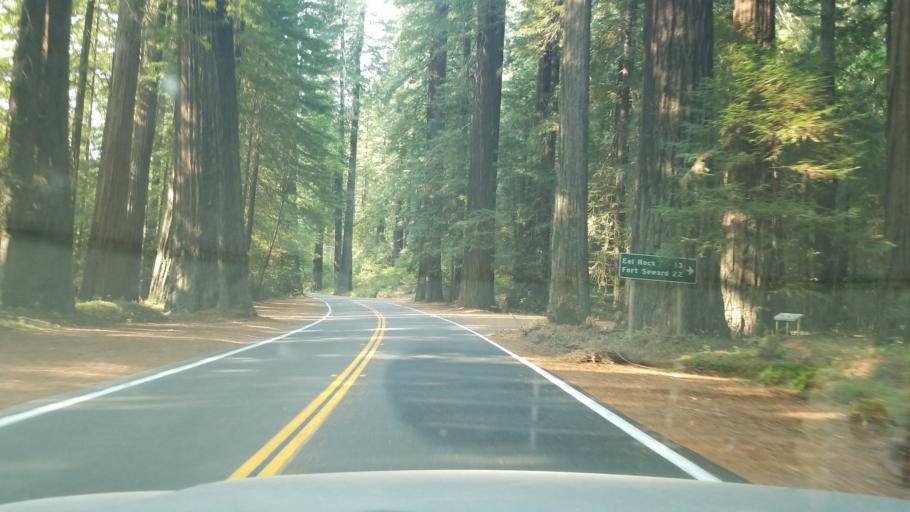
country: US
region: California
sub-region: Humboldt County
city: Redway
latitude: 40.2786
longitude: -123.8530
